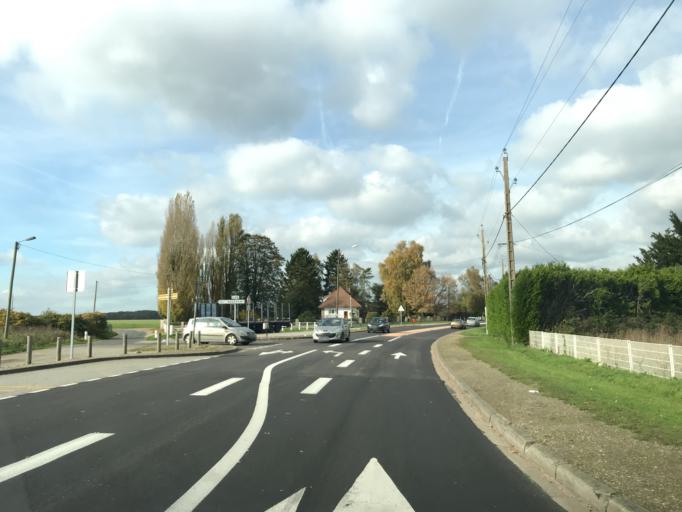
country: FR
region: Haute-Normandie
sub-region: Departement de l'Eure
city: Fleury-sur-Andelle
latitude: 49.3455
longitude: 1.3654
